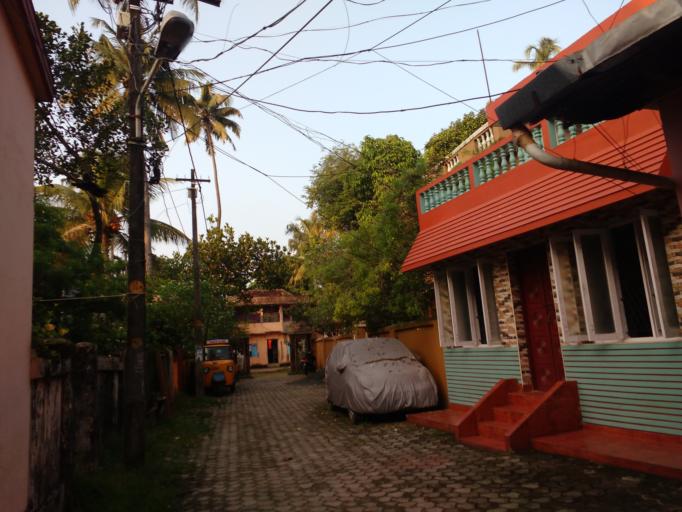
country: IN
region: Kerala
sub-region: Ernakulam
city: Cochin
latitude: 9.9599
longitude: 76.2504
